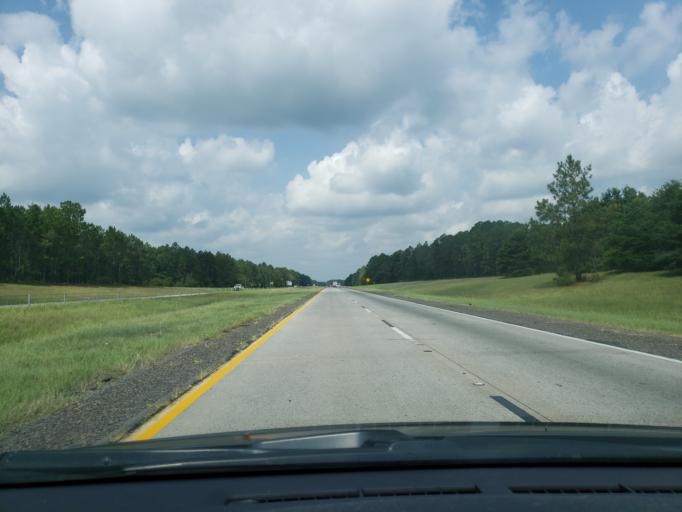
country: US
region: Georgia
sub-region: Treutlen County
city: Soperton
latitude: 32.4343
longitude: -82.6083
